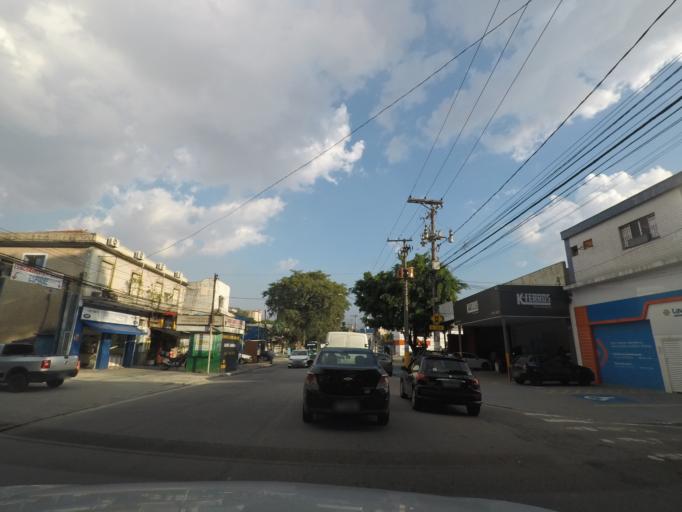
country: BR
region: Sao Paulo
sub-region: Sao Paulo
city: Sao Paulo
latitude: -23.5089
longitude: -46.6736
